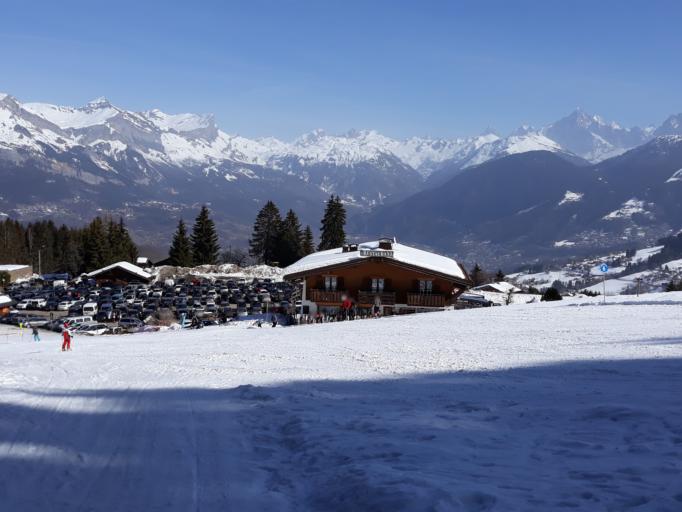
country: FR
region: Rhone-Alpes
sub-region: Departement de la Haute-Savoie
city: Combloux
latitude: 45.8876
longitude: 6.6210
